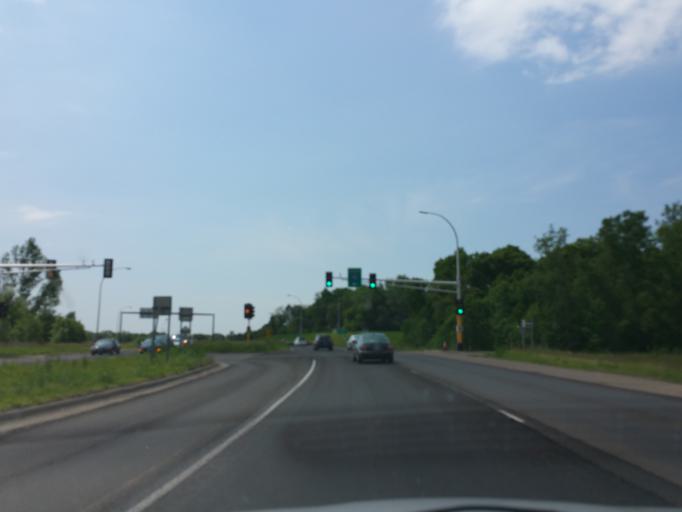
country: US
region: Minnesota
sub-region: Washington County
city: Lakeland
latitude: 44.9613
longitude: -92.7734
